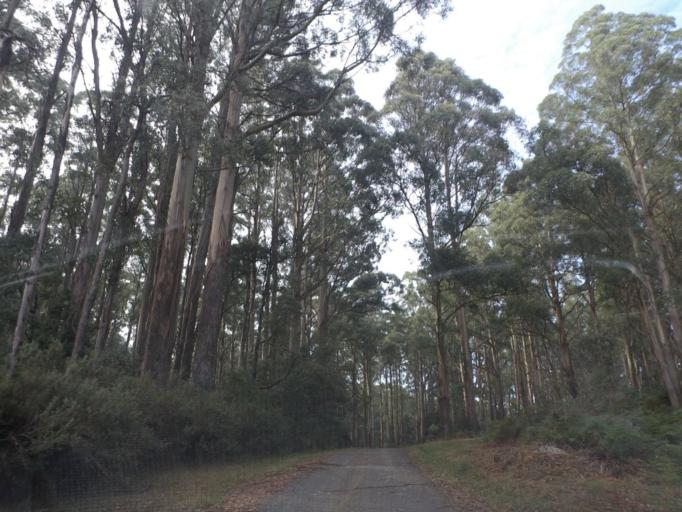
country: AU
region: Victoria
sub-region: Yarra Ranges
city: Healesville
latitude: -37.5729
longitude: 145.5440
